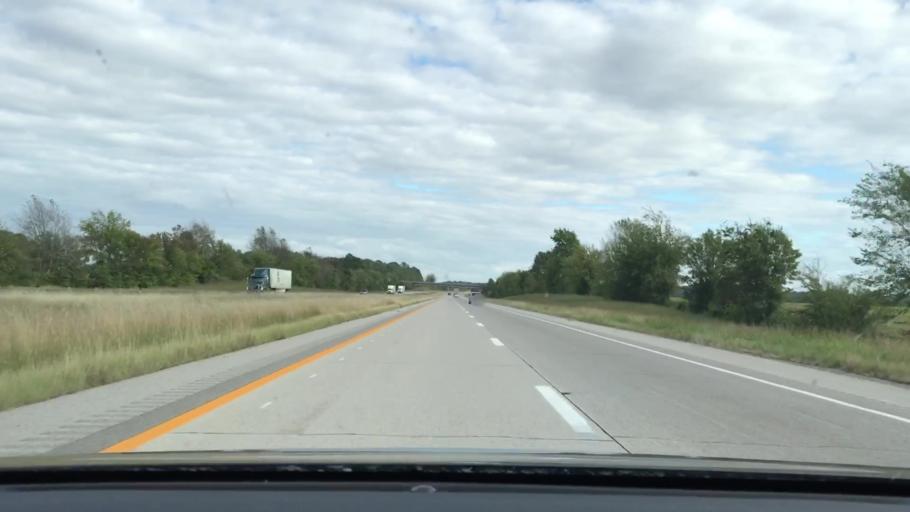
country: US
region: Kentucky
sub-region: Christian County
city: Hopkinsville
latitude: 36.7902
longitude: -87.5922
